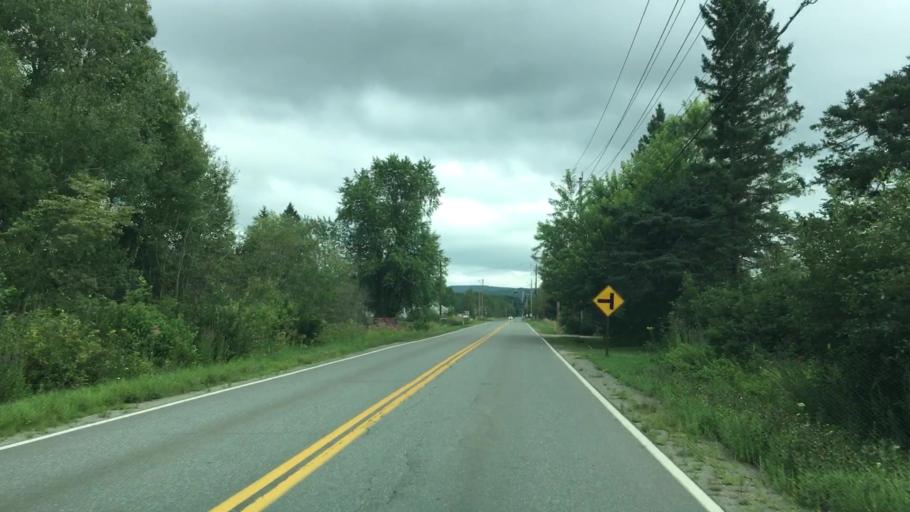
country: US
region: Maine
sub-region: Penobscot County
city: Brewer
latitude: 44.7657
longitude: -68.7521
